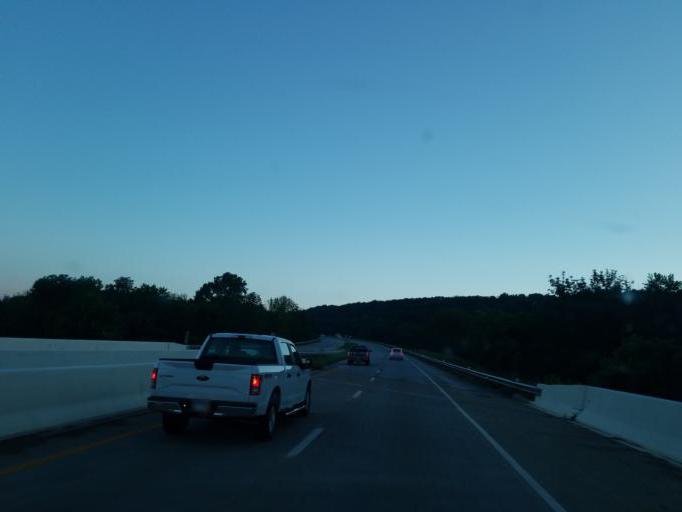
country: US
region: Ohio
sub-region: Summit County
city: Clinton
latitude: 40.9258
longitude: -81.6486
